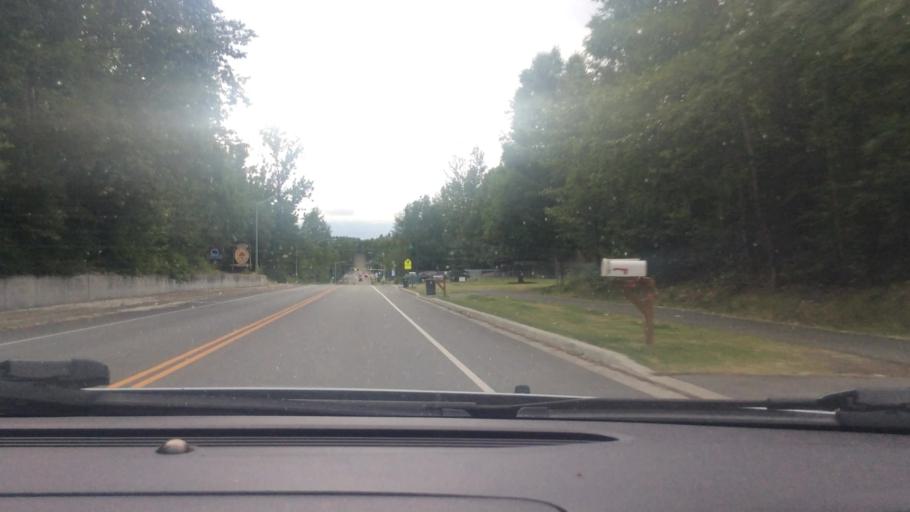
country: US
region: Alaska
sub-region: Anchorage Municipality
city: Anchorage
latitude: 61.1904
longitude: -149.7634
